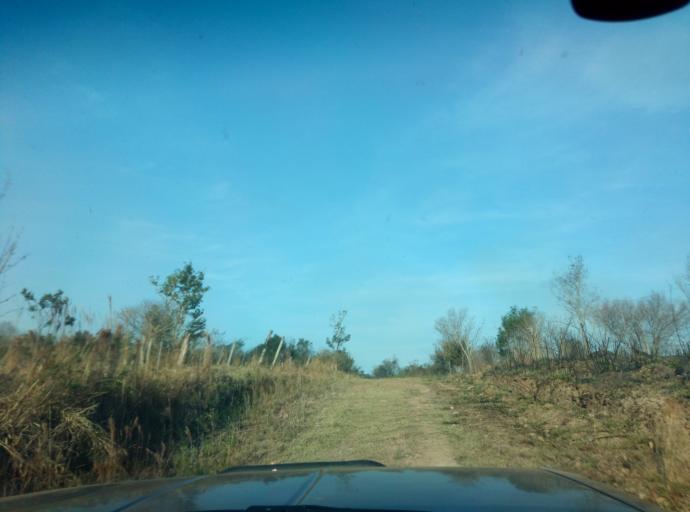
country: PY
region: Caaguazu
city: Doctor Cecilio Baez
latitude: -25.1998
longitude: -56.1190
